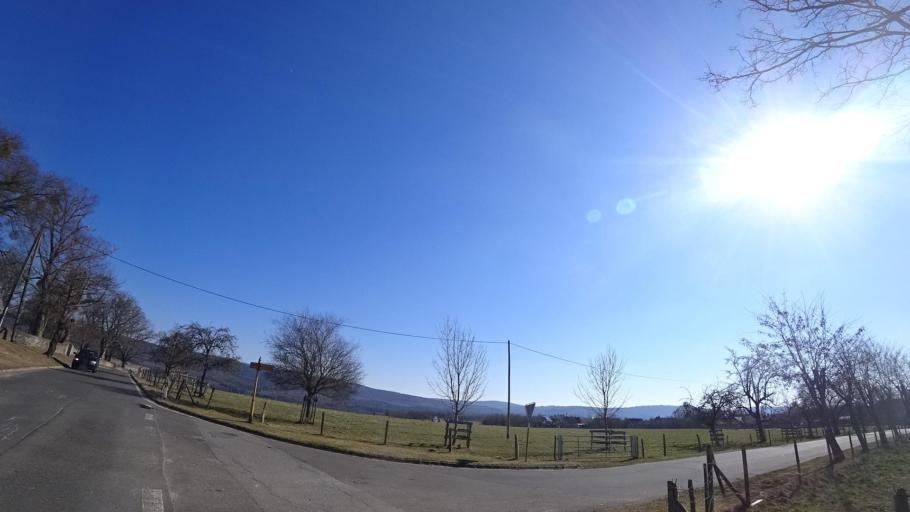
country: DE
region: Rheinland-Pfalz
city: Sargenroth
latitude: 49.9350
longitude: 7.5170
